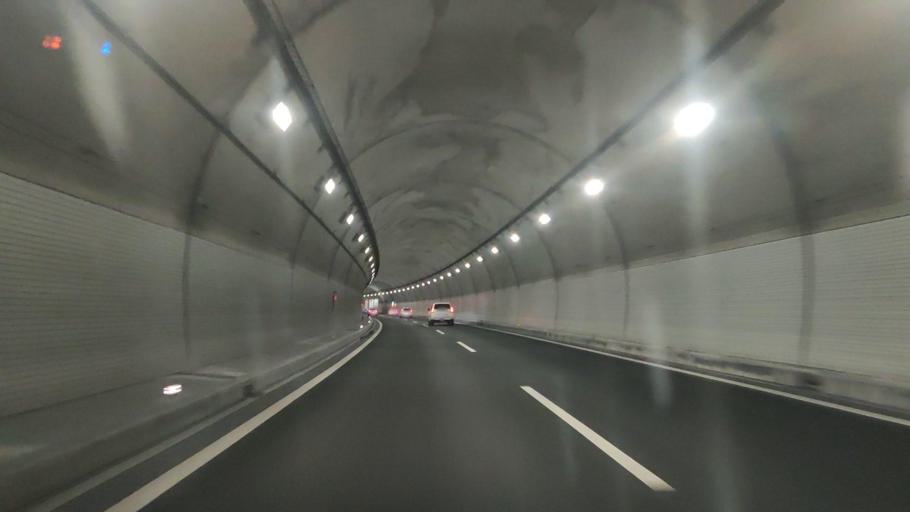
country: JP
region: Fukuoka
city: Kanda
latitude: 33.8030
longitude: 130.9459
